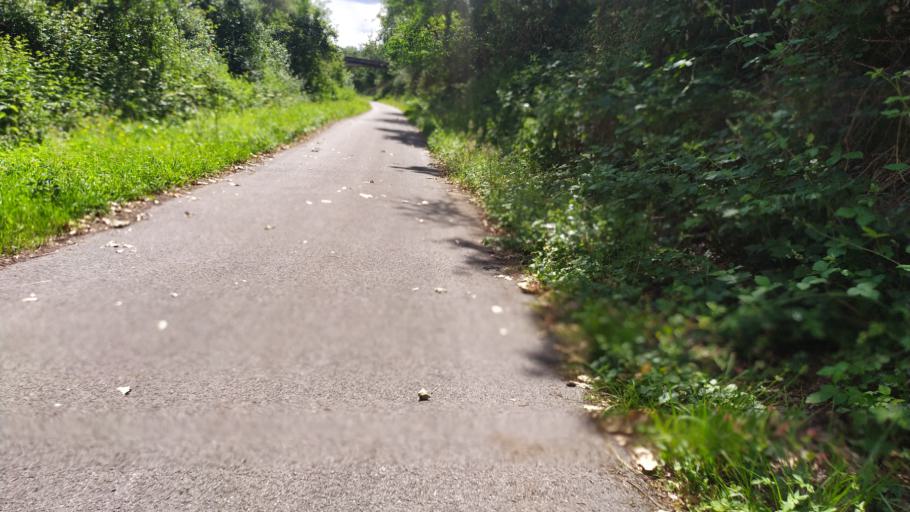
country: BE
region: Wallonia
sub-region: Province de Namur
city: Houyet
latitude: 50.1638
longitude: 5.0569
